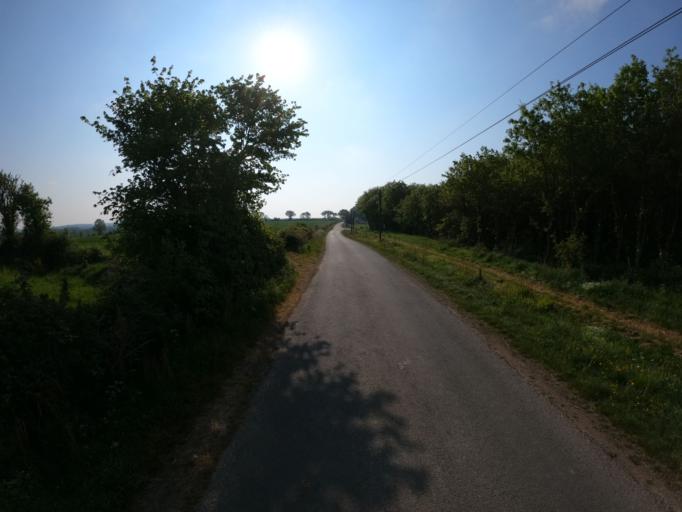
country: FR
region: Pays de la Loire
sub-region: Departement de Maine-et-Loire
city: Saint-Andre-de-la-Marche
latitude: 47.0721
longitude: -0.9879
